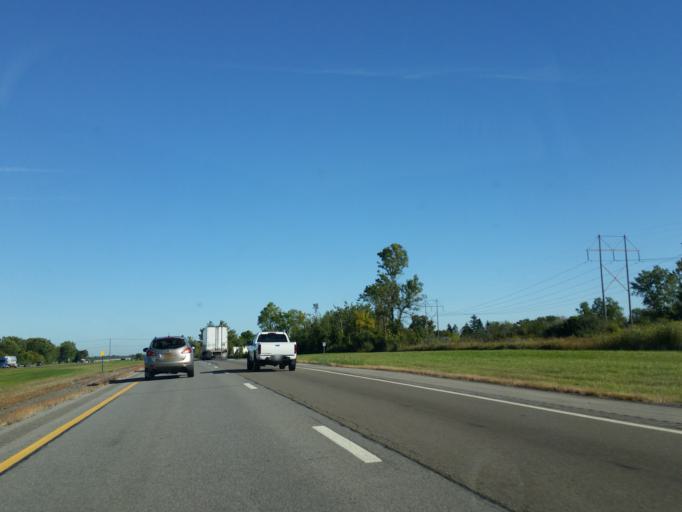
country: US
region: New York
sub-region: Erie County
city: Blasdell
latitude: 42.7765
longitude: -78.8158
